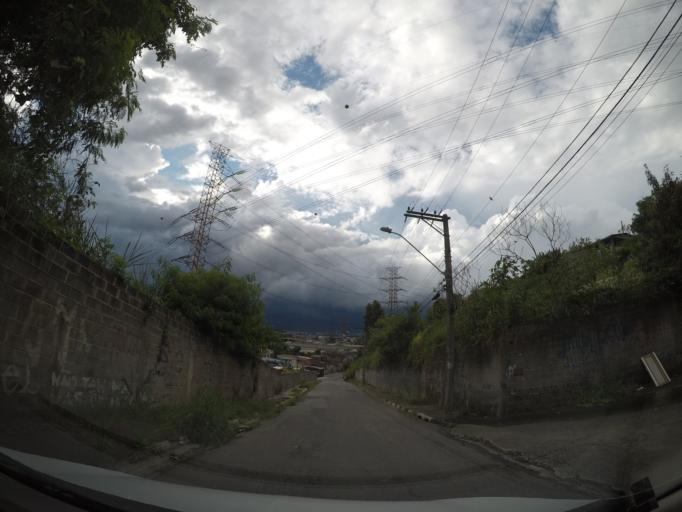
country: BR
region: Sao Paulo
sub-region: Guarulhos
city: Guarulhos
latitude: -23.4769
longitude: -46.5572
